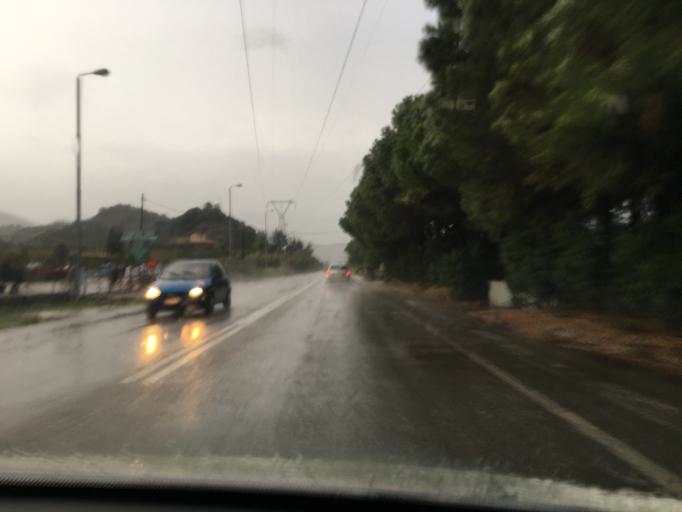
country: GR
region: West Greece
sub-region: Nomos Aitolias kai Akarnanias
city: Antirrio
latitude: 38.3492
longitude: 21.7720
